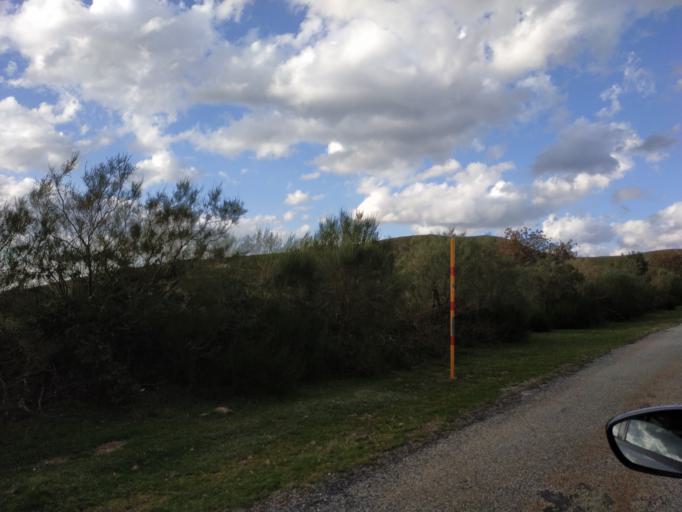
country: ES
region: Castille and Leon
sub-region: Provincia de Leon
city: Candin
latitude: 42.8782
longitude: -6.8306
